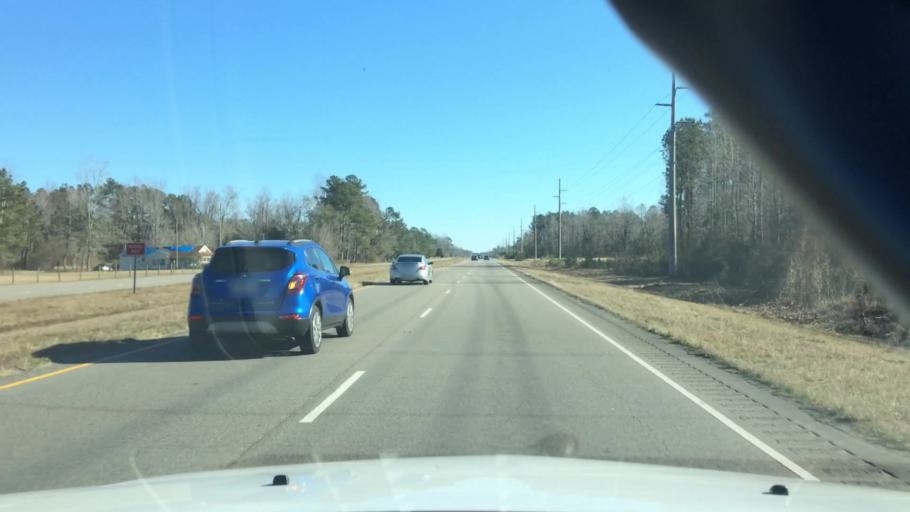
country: US
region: North Carolina
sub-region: Brunswick County
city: Shallotte
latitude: 34.0032
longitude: -78.3128
